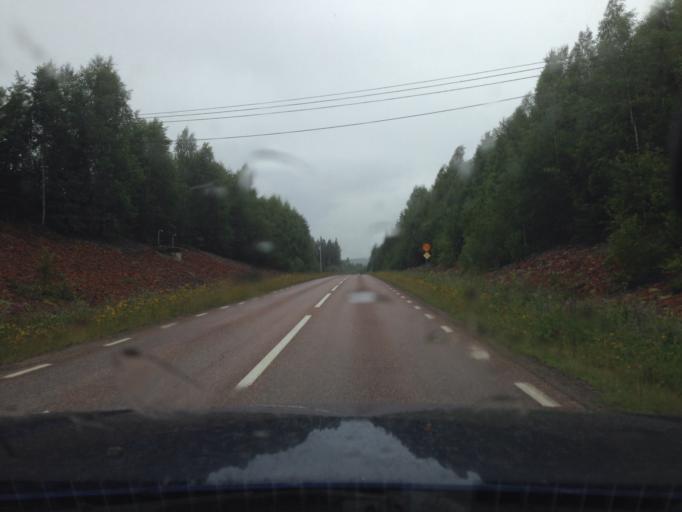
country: SE
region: Dalarna
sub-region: Ludvika Kommun
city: Grangesberg
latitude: 60.1322
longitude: 15.0543
